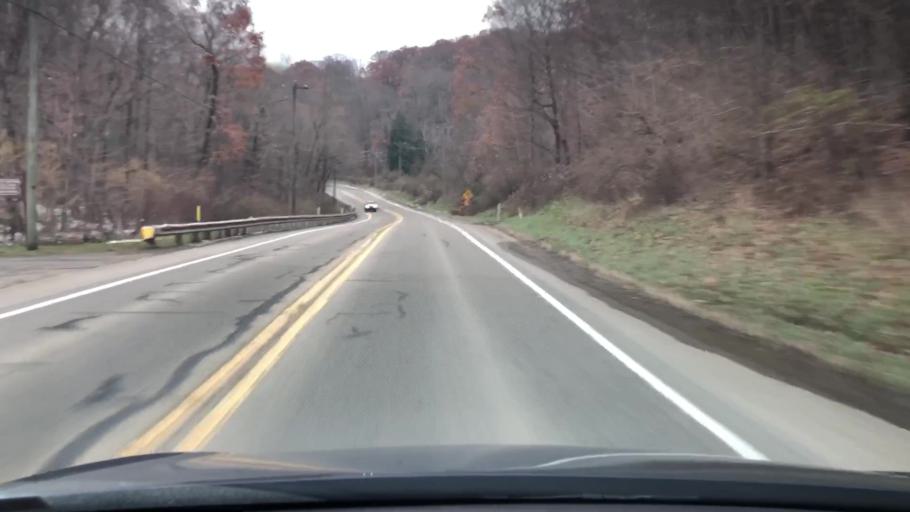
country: US
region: Pennsylvania
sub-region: Clarion County
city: Clarion
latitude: 40.9886
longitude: -79.3452
